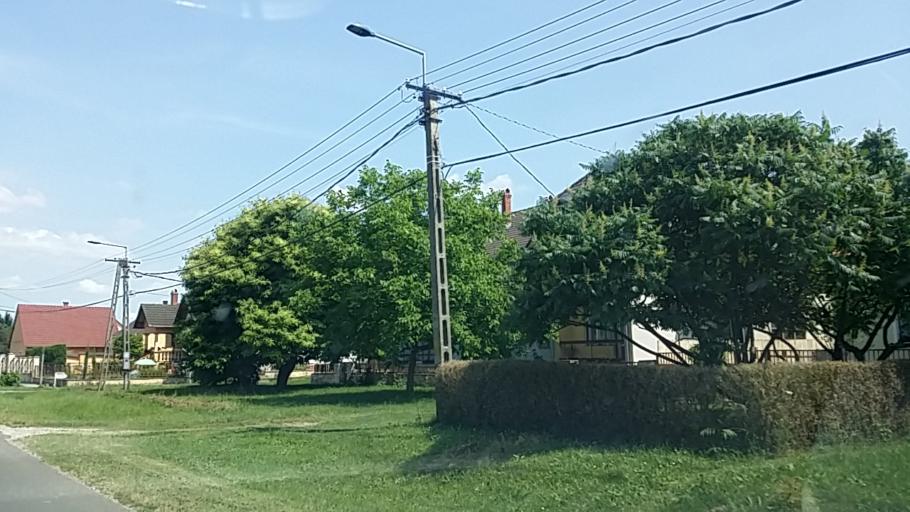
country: HU
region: Baranya
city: Harkany
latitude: 45.8460
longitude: 18.2317
